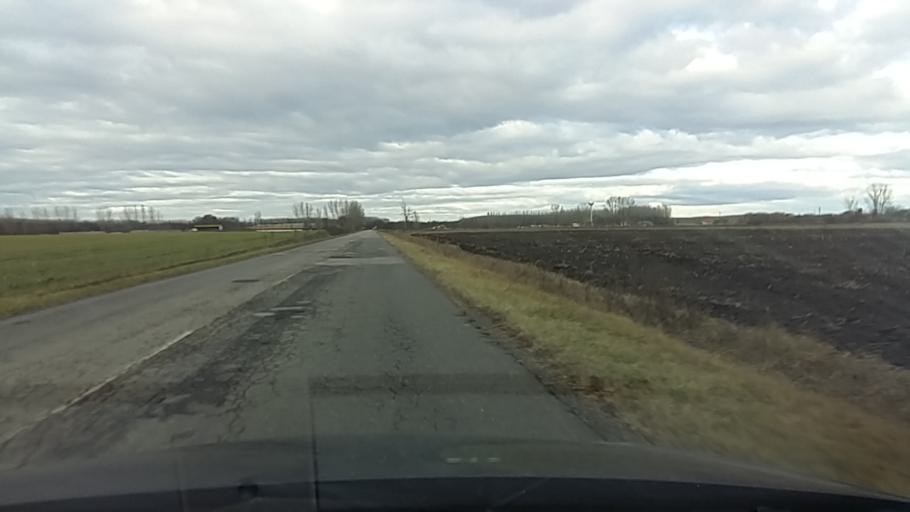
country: HU
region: Szabolcs-Szatmar-Bereg
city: Nyirbogdany
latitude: 48.0537
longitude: 21.8612
